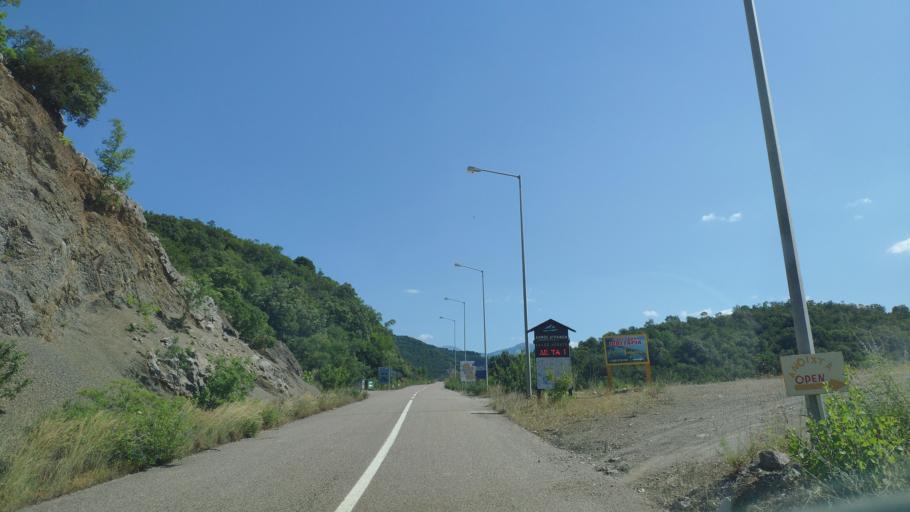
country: GR
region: Central Greece
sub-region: Nomos Evrytanias
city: Kerasochori
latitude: 38.9741
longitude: 21.4930
